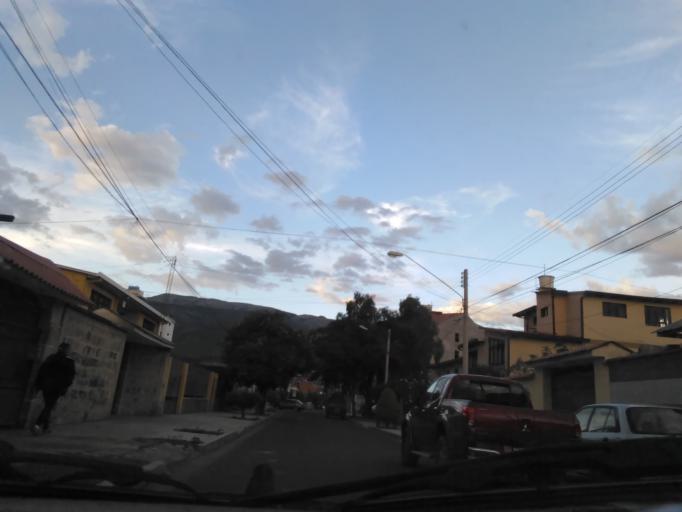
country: BO
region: Cochabamba
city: Cochabamba
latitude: -17.3863
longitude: -66.1676
